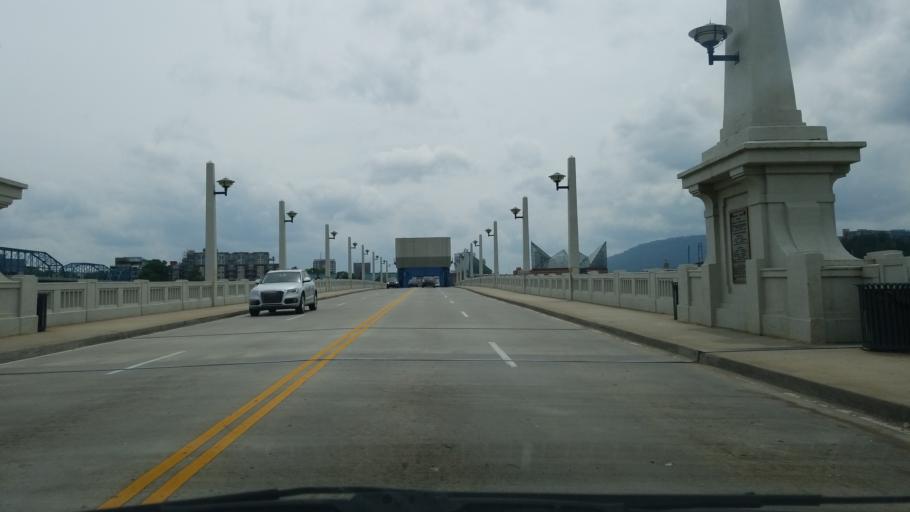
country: US
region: Tennessee
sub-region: Hamilton County
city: Chattanooga
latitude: 35.0606
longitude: -85.3089
